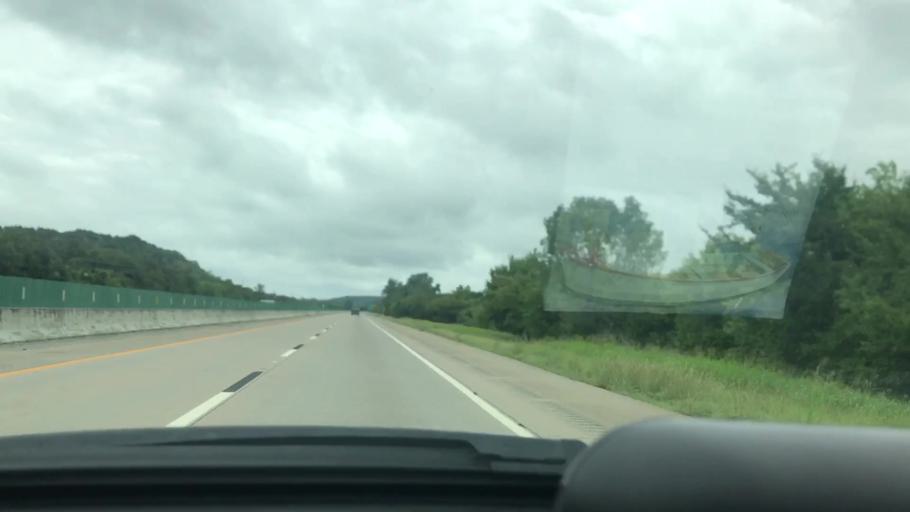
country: US
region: Oklahoma
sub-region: Pittsburg County
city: Krebs
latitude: 35.0875
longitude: -95.7010
